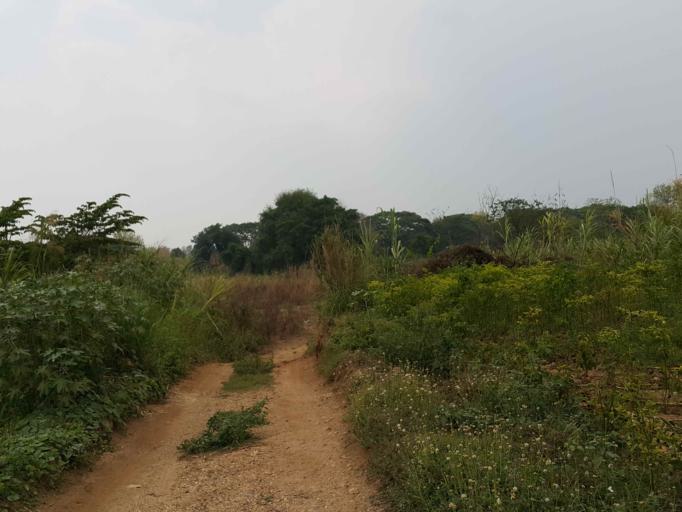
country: TH
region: Chiang Mai
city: Mae Taeng
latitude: 19.1196
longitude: 98.9949
